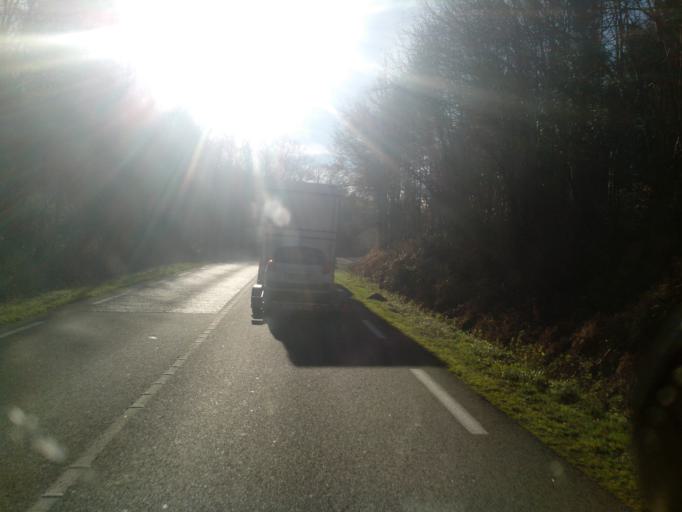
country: FR
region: Limousin
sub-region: Departement de la Haute-Vienne
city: Nantiat
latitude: 46.0551
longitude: 1.1201
